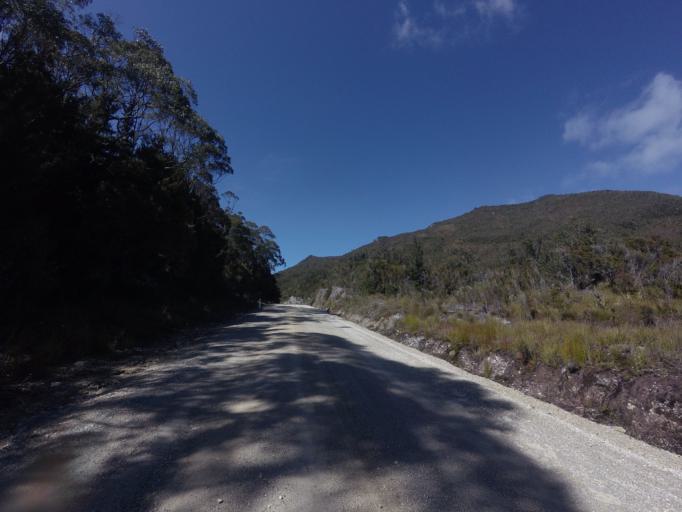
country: AU
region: Tasmania
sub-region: Huon Valley
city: Geeveston
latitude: -42.8149
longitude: 146.3858
